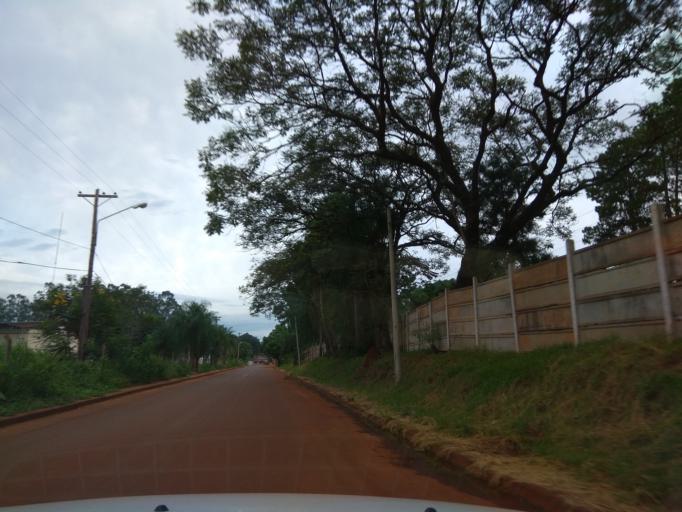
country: AR
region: Misiones
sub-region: Departamento de Capital
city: Posadas
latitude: -27.4382
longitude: -55.8894
